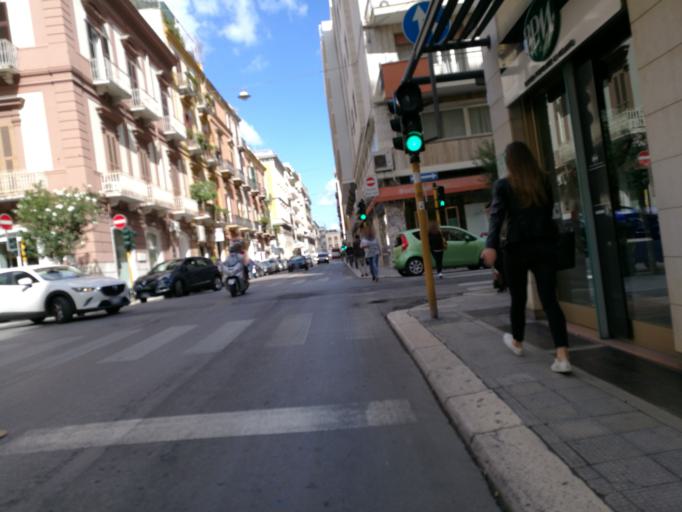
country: IT
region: Apulia
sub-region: Provincia di Bari
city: Bari
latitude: 41.1231
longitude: 16.8690
